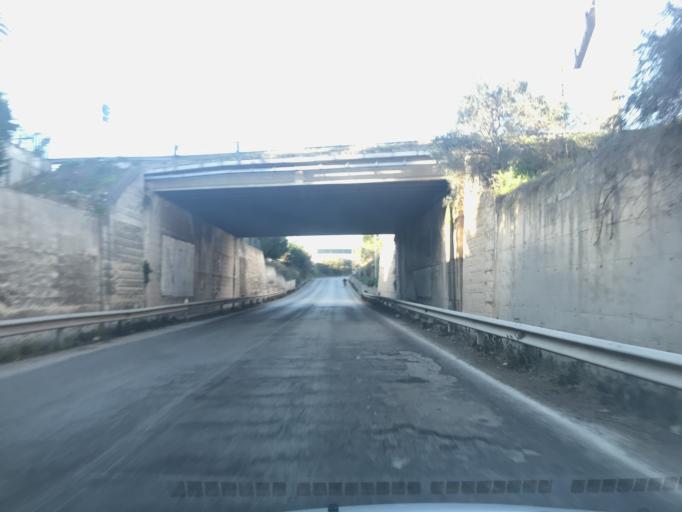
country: IT
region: Apulia
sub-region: Provincia di Bari
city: Corato
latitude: 41.1362
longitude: 16.4158
